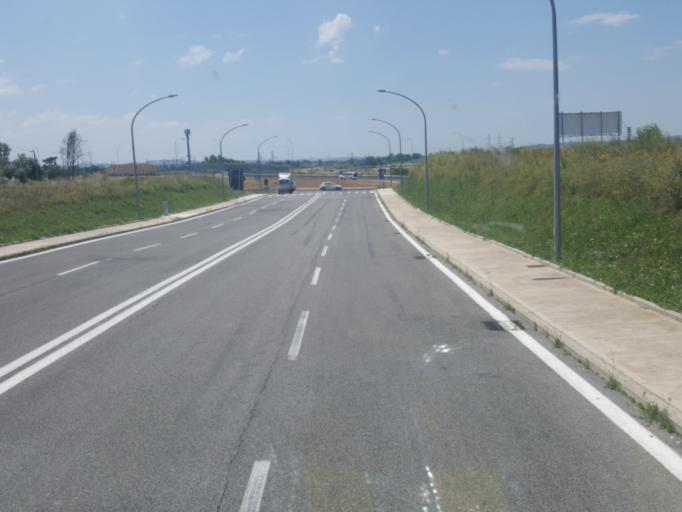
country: IT
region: Latium
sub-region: Citta metropolitana di Roma Capitale
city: Fiano Romano
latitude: 42.1644
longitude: 12.6479
